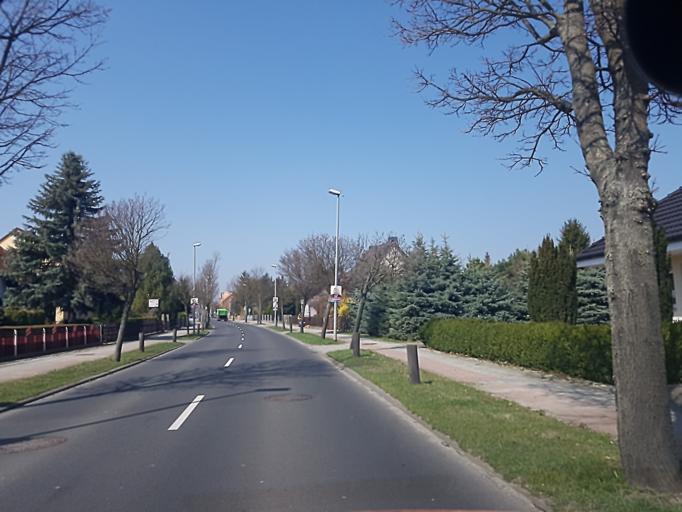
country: DE
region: Brandenburg
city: Tschernitz
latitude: 51.6114
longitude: 14.6049
